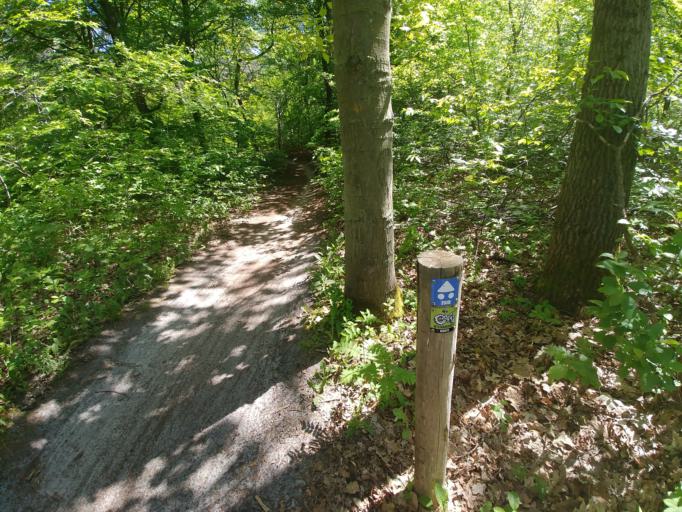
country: NL
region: North Holland
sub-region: Gemeente Bergen
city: Egmond aan Zee
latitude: 52.6823
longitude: 4.6659
